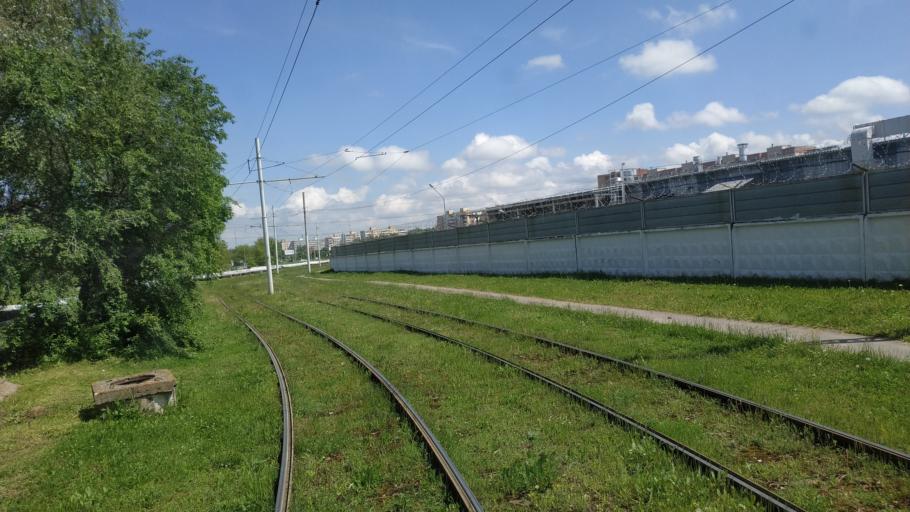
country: RU
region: Moskovskaya
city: Sychevo
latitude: 55.0602
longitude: 38.7350
